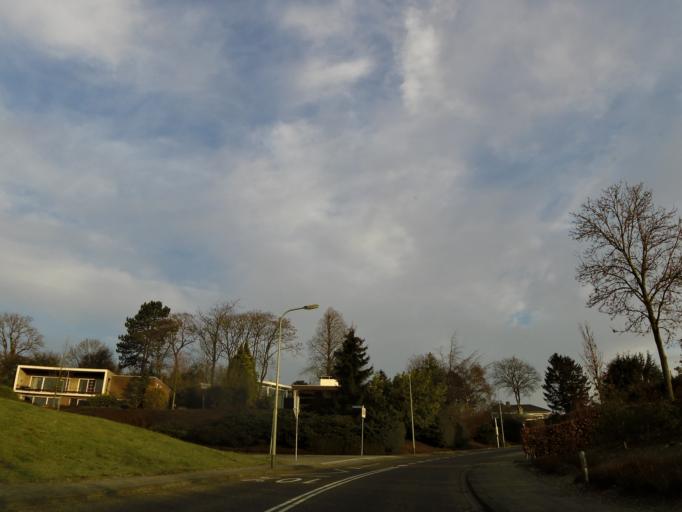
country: NL
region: Limburg
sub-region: Gemeente Simpelveld
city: Simpelveld
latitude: 50.8393
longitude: 5.9747
